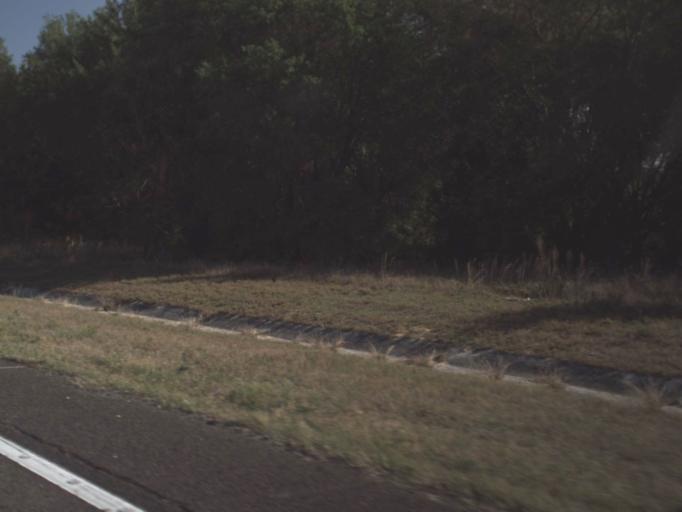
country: US
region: Florida
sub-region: Lake County
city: Minneola
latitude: 28.6138
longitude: -81.7589
